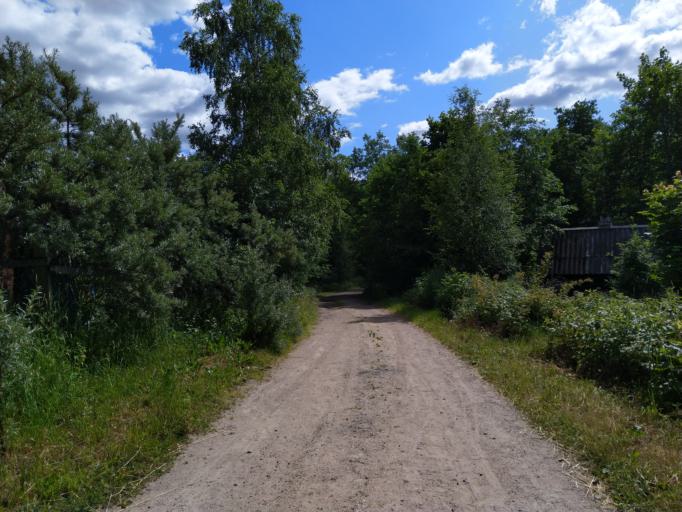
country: RU
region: Leningrad
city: Sapernoye
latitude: 60.6805
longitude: 30.0086
